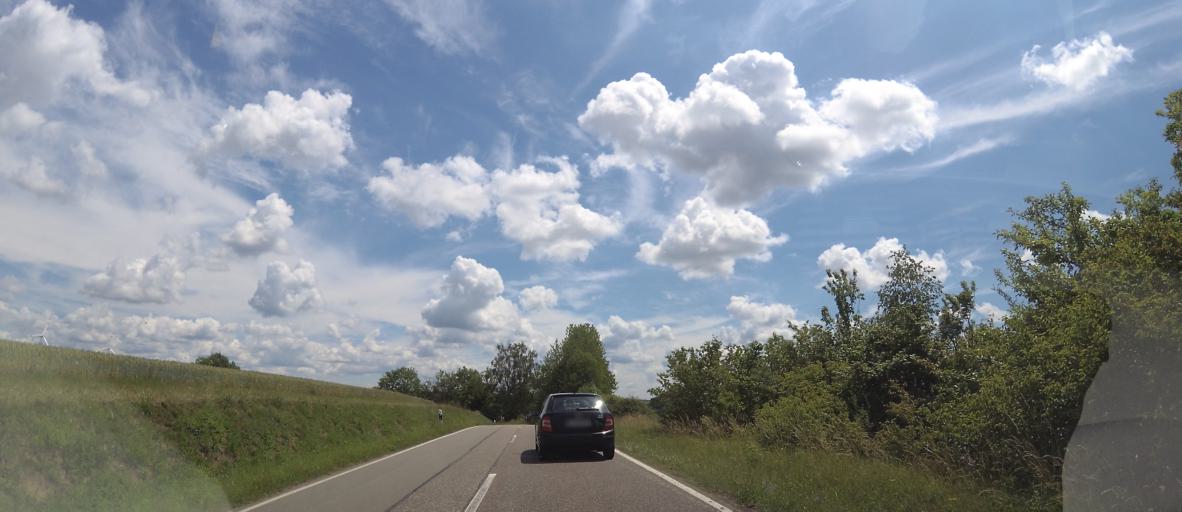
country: DE
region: Rheinland-Pfalz
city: Walshausen
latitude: 49.2168
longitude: 7.4698
